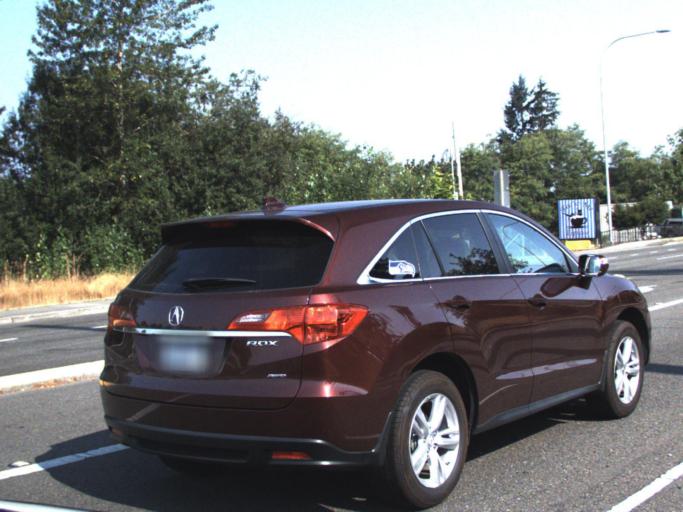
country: US
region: Washington
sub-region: King County
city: Federal Way
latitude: 47.3393
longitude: -122.3121
